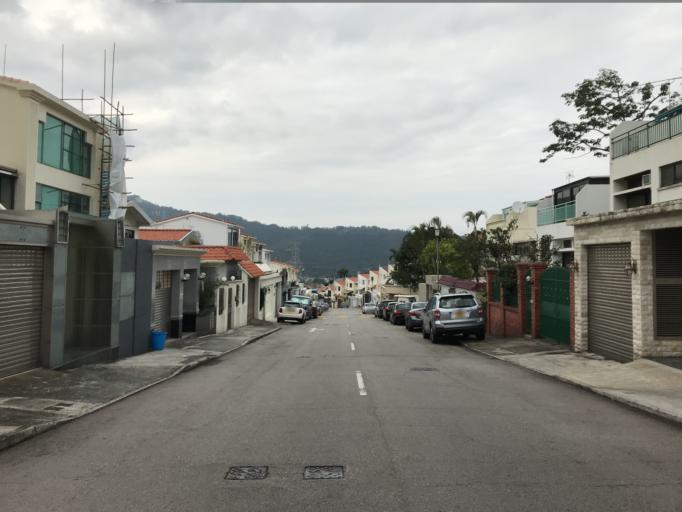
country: HK
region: Tai Po
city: Tai Po
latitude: 22.4643
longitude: 114.1591
